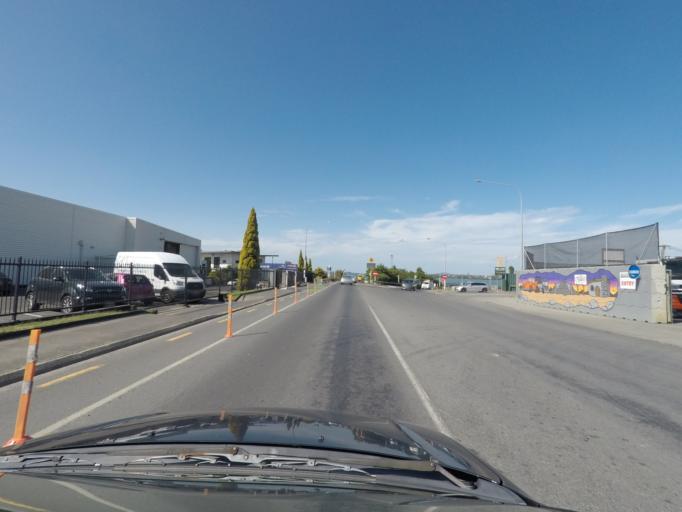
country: NZ
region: Auckland
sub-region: Auckland
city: Rosebank
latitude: -36.8706
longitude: 174.6721
